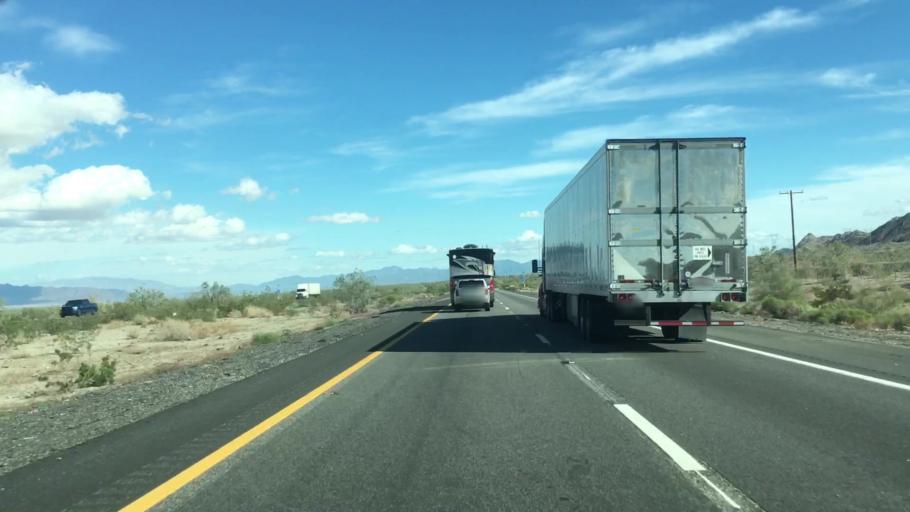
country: US
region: California
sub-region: Imperial County
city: Niland
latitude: 33.6906
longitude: -115.5052
